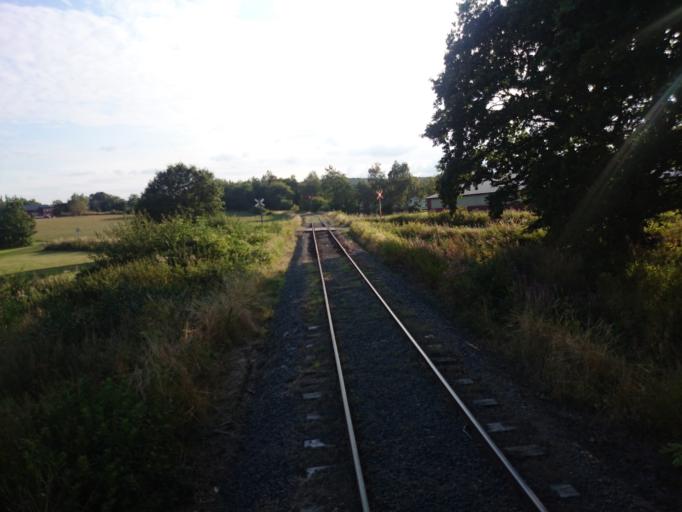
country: SE
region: Skane
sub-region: Simrishamns Kommun
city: Kivik
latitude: 55.6896
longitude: 14.1586
